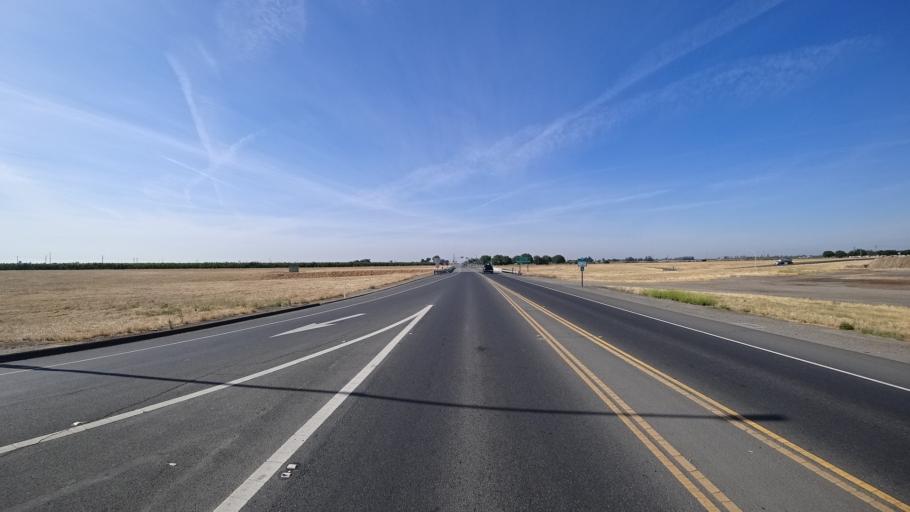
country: US
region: California
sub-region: Kings County
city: Home Garden
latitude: 36.3262
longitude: -119.6009
